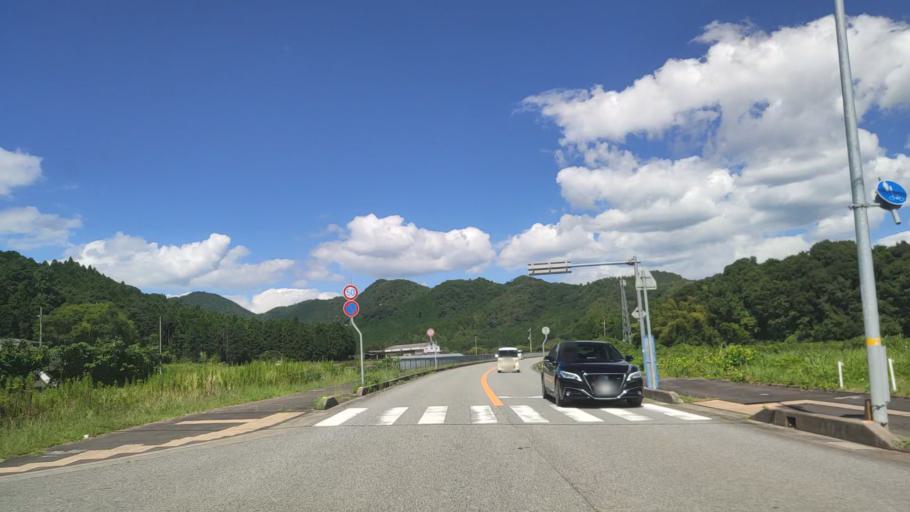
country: JP
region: Kyoto
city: Fukuchiyama
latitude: 35.2402
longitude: 135.1233
